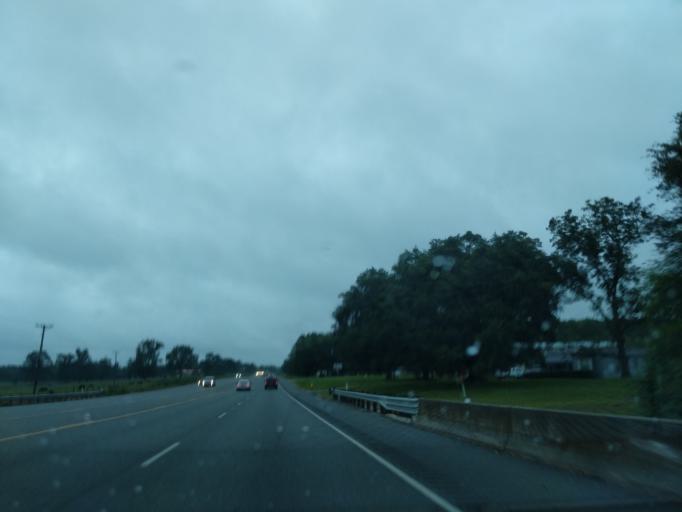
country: US
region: Texas
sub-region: Angelina County
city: Redland
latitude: 31.3889
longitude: -94.7154
